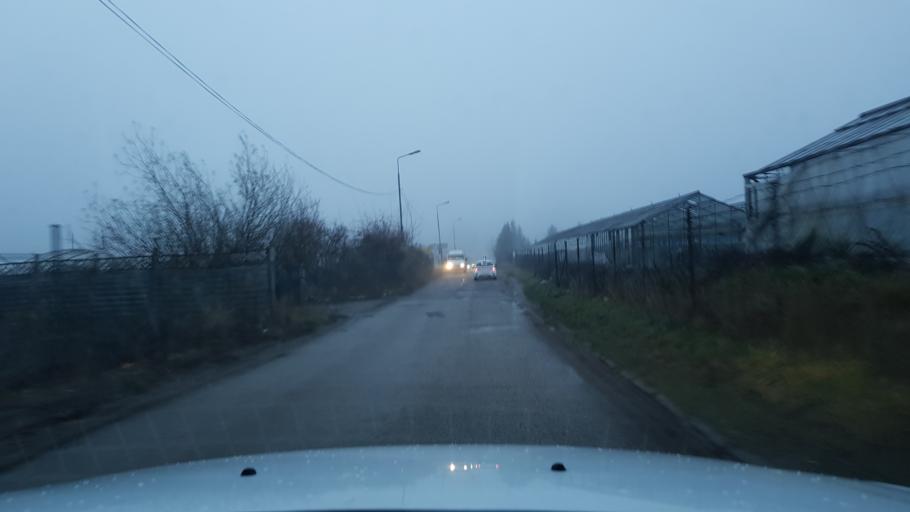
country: PL
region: West Pomeranian Voivodeship
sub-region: Powiat policki
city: Przeclaw
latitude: 53.3893
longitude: 14.4882
